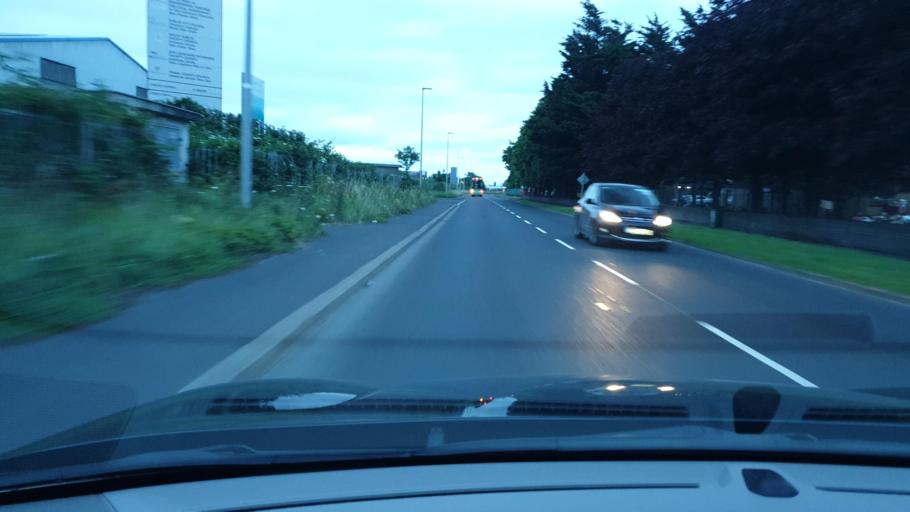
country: IE
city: Cherry Orchard
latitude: 53.3133
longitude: -6.3583
